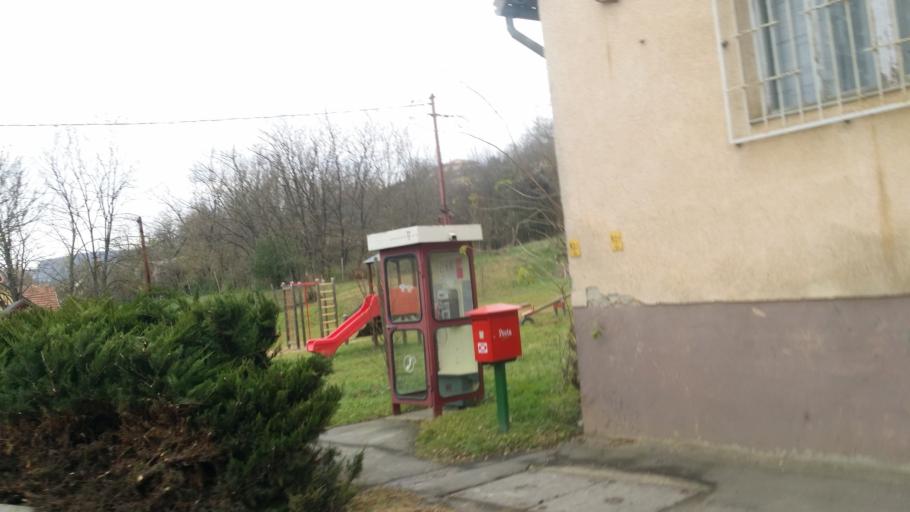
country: HU
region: Tolna
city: Szentgalpuszta
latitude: 46.2746
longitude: 18.6369
